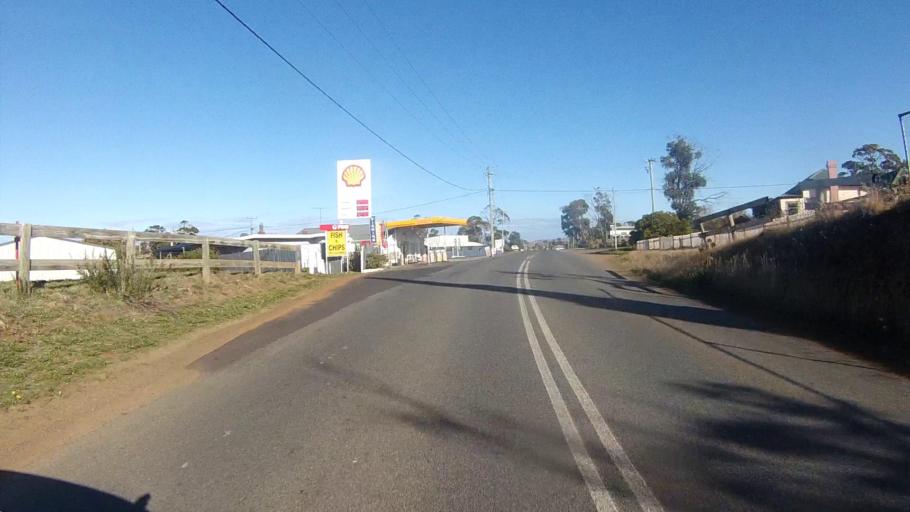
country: AU
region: Tasmania
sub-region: Sorell
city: Sorell
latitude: -42.8846
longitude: 147.8140
